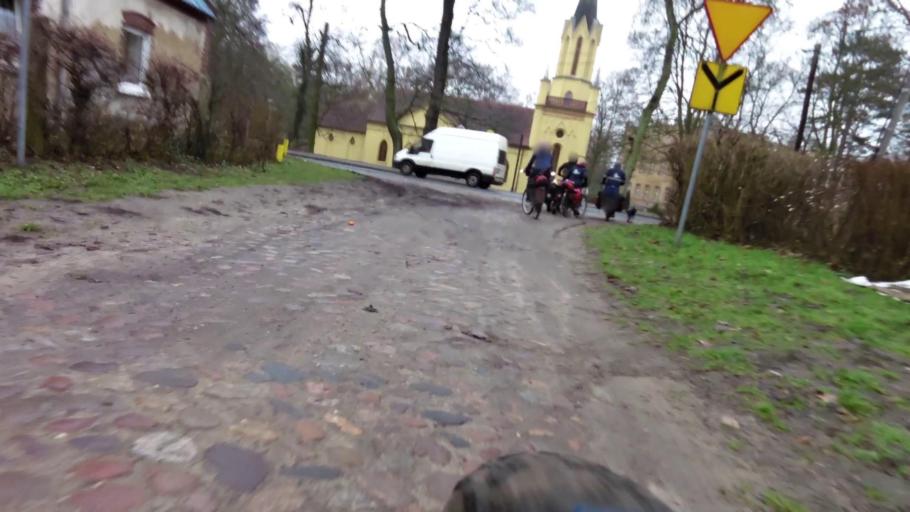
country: PL
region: Lubusz
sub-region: Powiat gorzowski
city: Kostrzyn nad Odra
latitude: 52.6206
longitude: 14.7051
